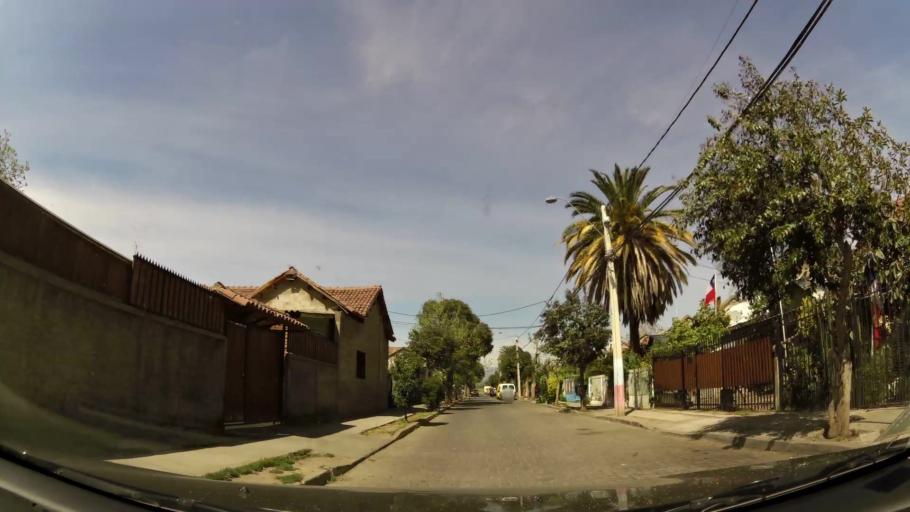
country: CL
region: Santiago Metropolitan
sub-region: Provincia de Cordillera
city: Puente Alto
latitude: -33.6181
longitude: -70.5666
